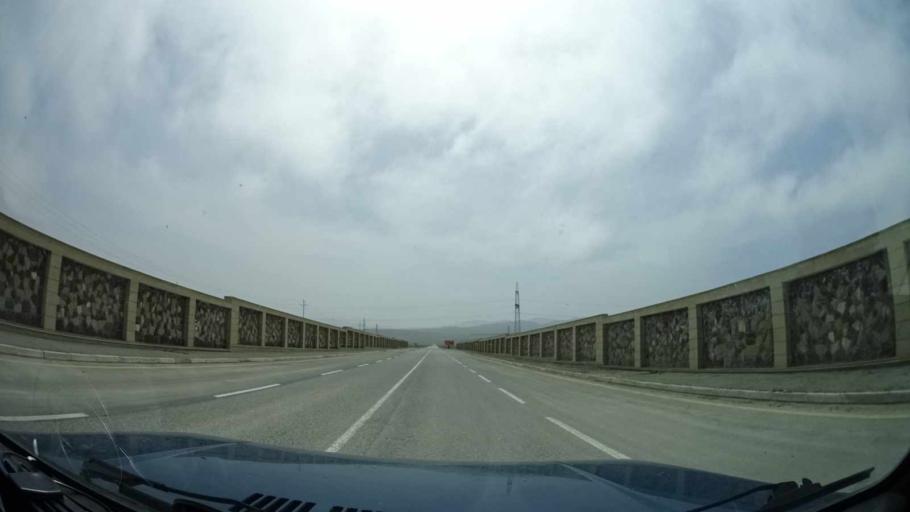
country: AZ
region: Xizi
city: Kilyazi
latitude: 40.8667
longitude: 49.3388
